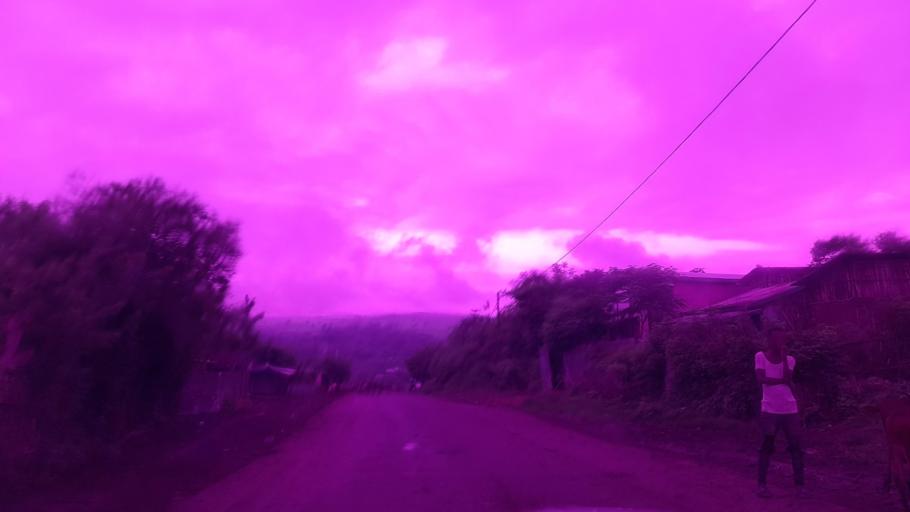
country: ET
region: Oromiya
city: Waliso
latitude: 8.2267
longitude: 37.5763
